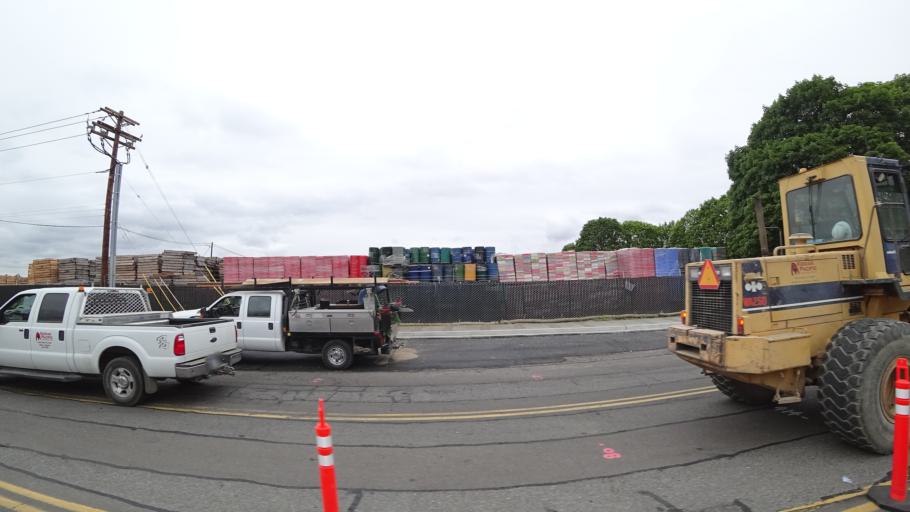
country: US
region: Oregon
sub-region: Multnomah County
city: Wood Village
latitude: 45.5430
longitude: -122.4225
